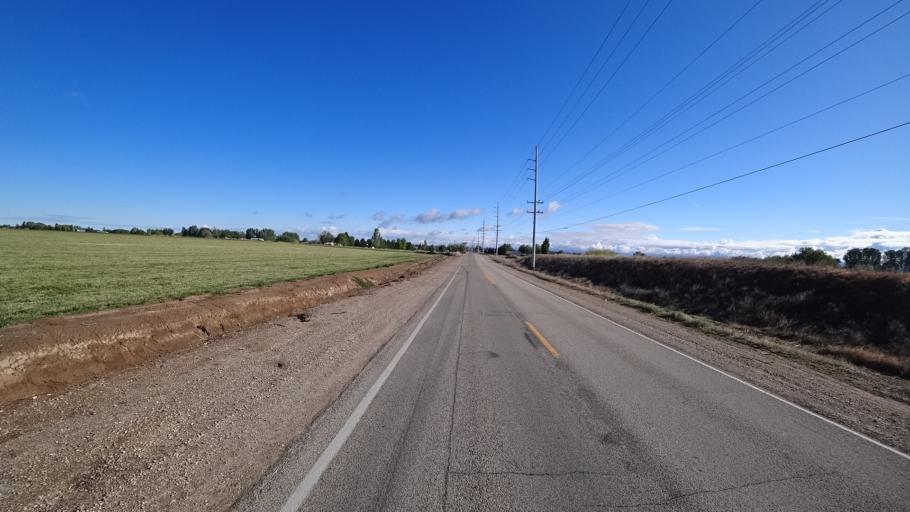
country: US
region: Idaho
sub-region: Ada County
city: Kuna
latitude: 43.4691
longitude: -116.4137
